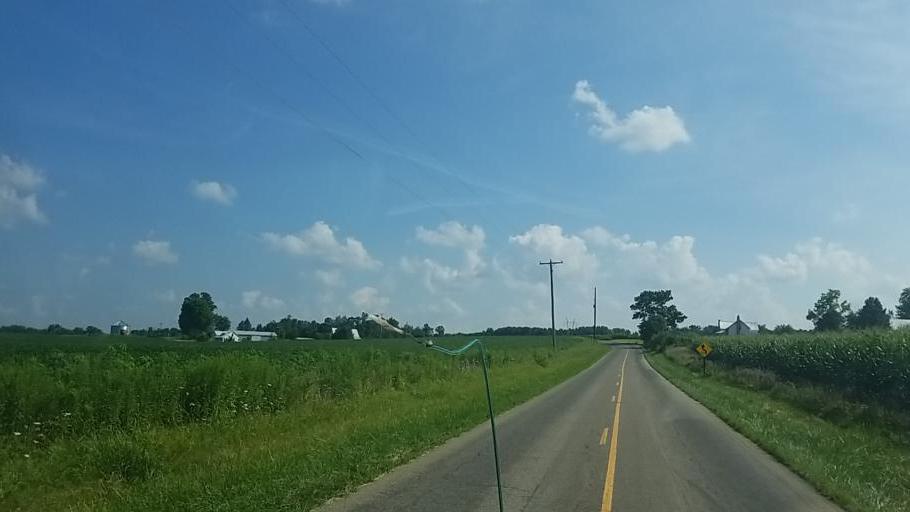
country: US
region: Ohio
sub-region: Knox County
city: Oak Hill
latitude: 40.3348
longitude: -82.2742
